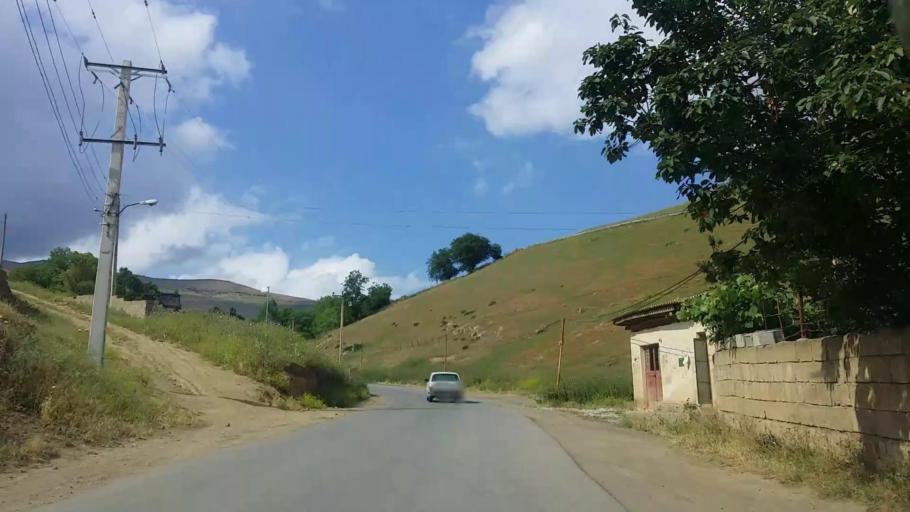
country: IR
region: Mazandaran
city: Chalus
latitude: 36.5165
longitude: 51.2594
